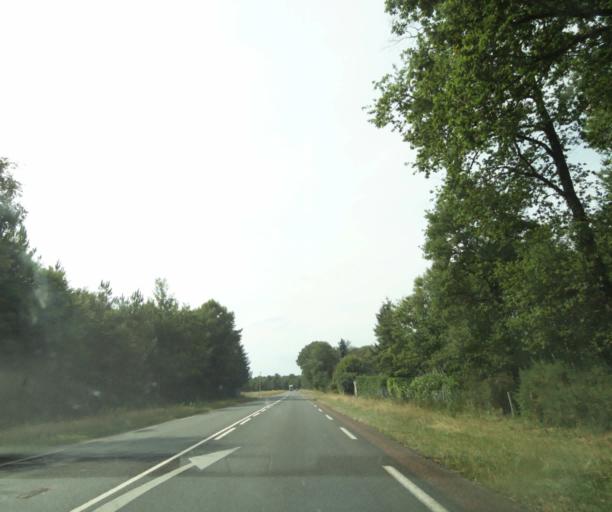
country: FR
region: Pays de la Loire
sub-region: Departement de la Sarthe
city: Marigne-Laille
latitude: 47.8004
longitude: 0.3272
